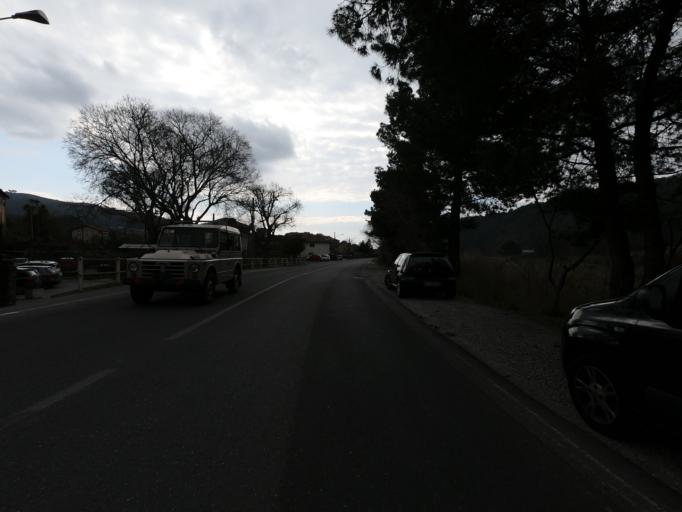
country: IT
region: Liguria
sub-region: Provincia di Imperia
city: Villa Faraldi
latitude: 43.9918
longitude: 8.1214
